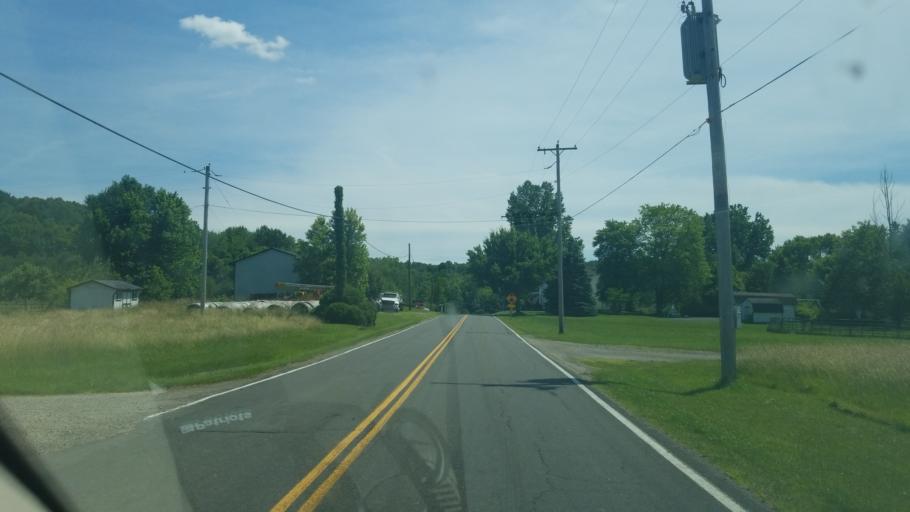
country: US
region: Ohio
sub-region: Stark County
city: Brewster
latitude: 40.7083
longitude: -81.5725
